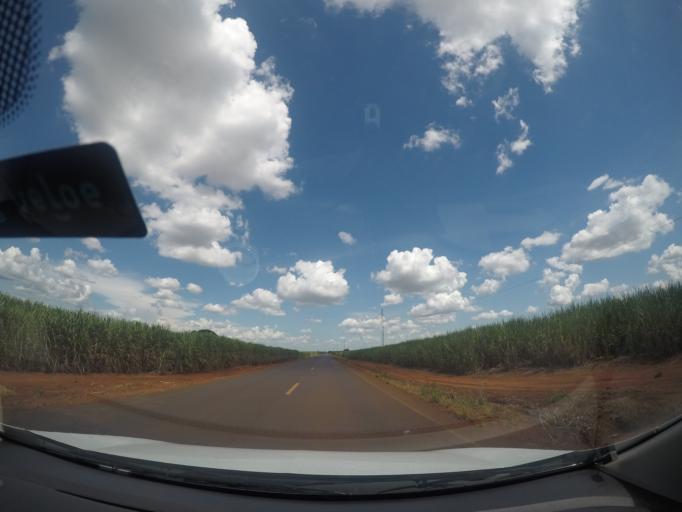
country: BR
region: Minas Gerais
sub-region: Frutal
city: Frutal
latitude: -19.8517
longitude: -48.7358
